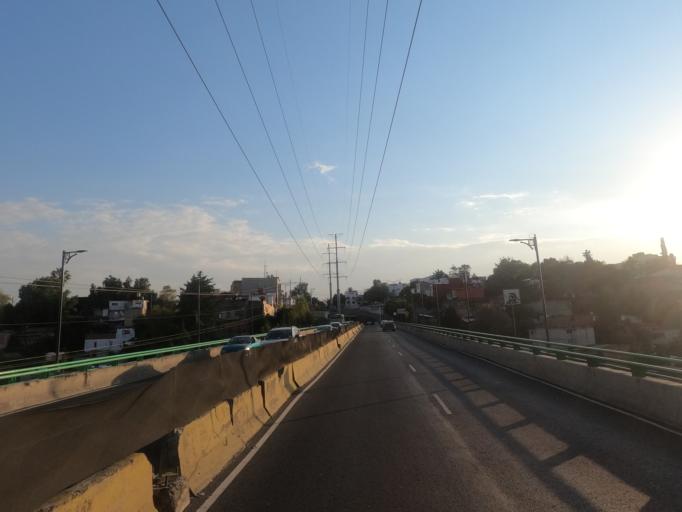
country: MX
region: Mexico City
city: Alvaro Obregon
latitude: 19.3619
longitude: -99.2059
